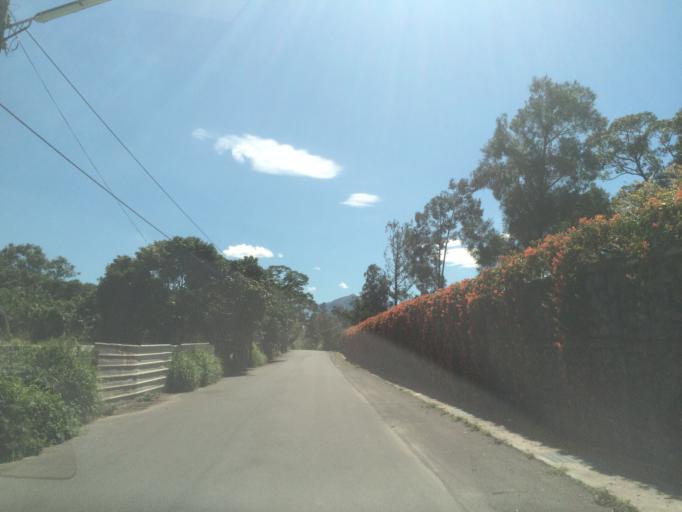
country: TW
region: Taiwan
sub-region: Yunlin
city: Douliu
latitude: 23.7044
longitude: 120.6098
